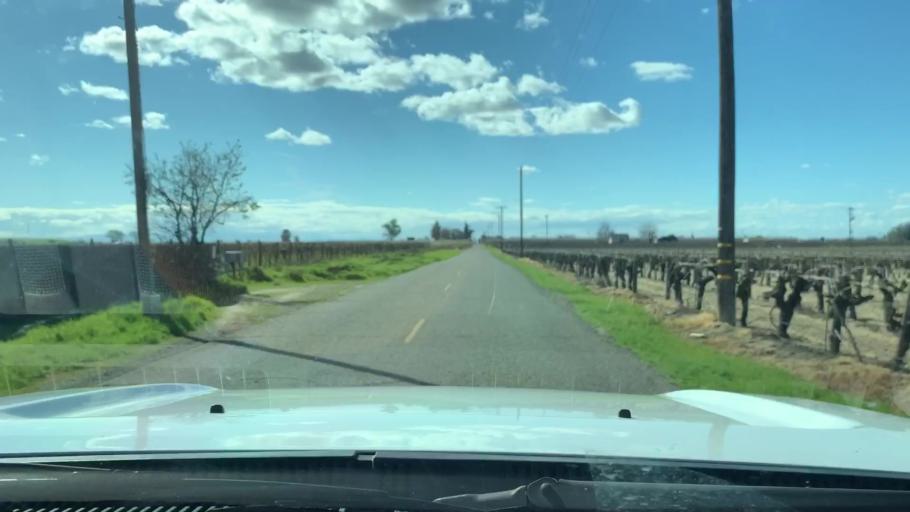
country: US
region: California
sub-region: Fresno County
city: Fowler
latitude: 36.5618
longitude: -119.7163
